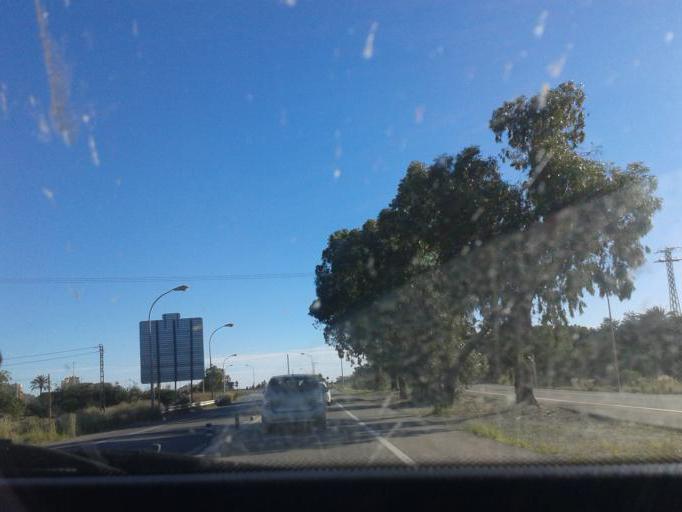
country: ES
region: Valencia
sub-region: Provincia de Alicante
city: San Juan de Alicante
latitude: 38.4159
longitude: -0.4231
